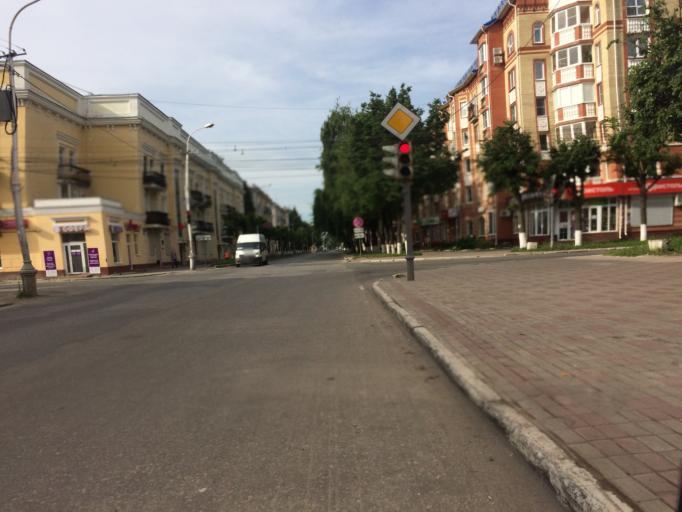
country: RU
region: Mariy-El
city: Yoshkar-Ola
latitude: 56.6327
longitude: 47.8957
